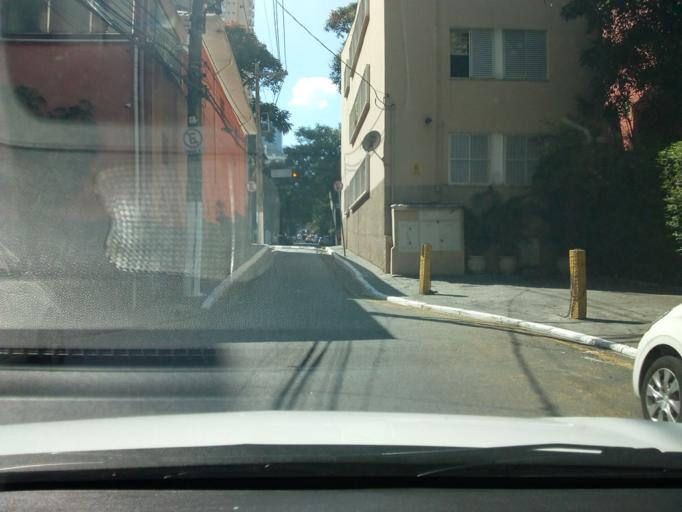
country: BR
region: Sao Paulo
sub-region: Sao Paulo
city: Sao Paulo
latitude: -23.5738
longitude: -46.6504
